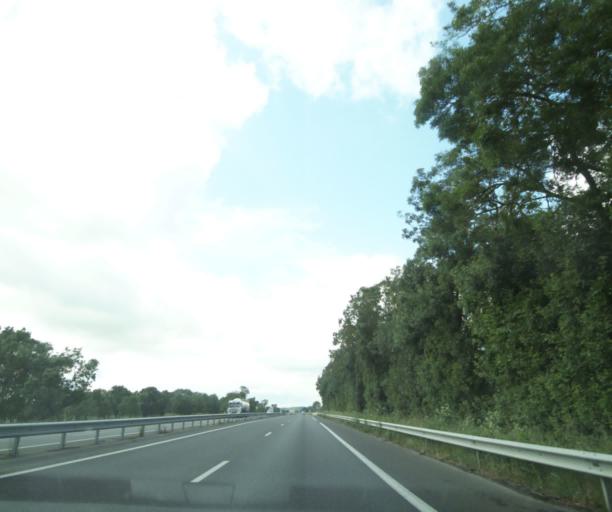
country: FR
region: Pays de la Loire
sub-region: Departement de Maine-et-Loire
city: Vivy
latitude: 47.2949
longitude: -0.0411
